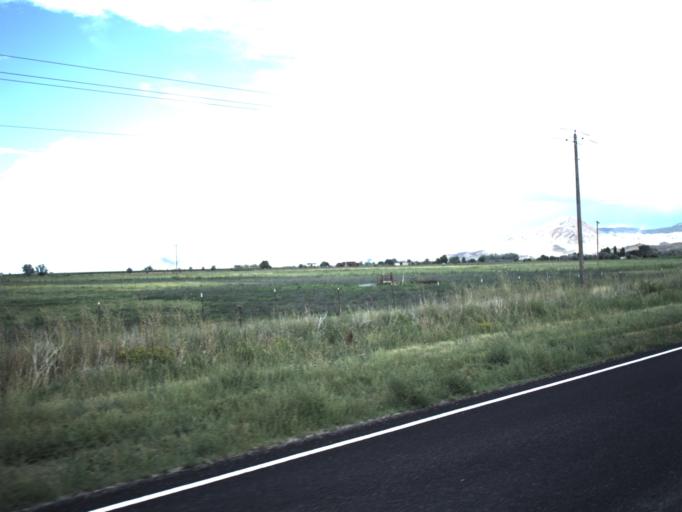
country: US
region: Utah
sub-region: Sevier County
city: Richfield
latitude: 38.7731
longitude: -112.0483
